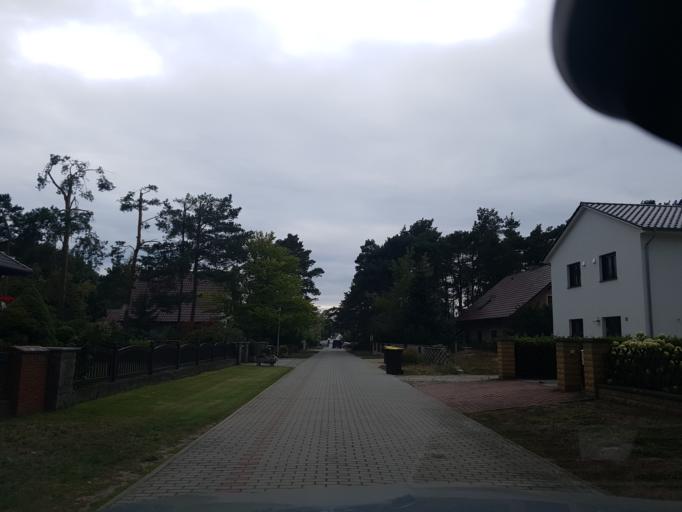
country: DE
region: Brandenburg
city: Bad Liebenwerda
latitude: 51.5004
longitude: 13.4303
